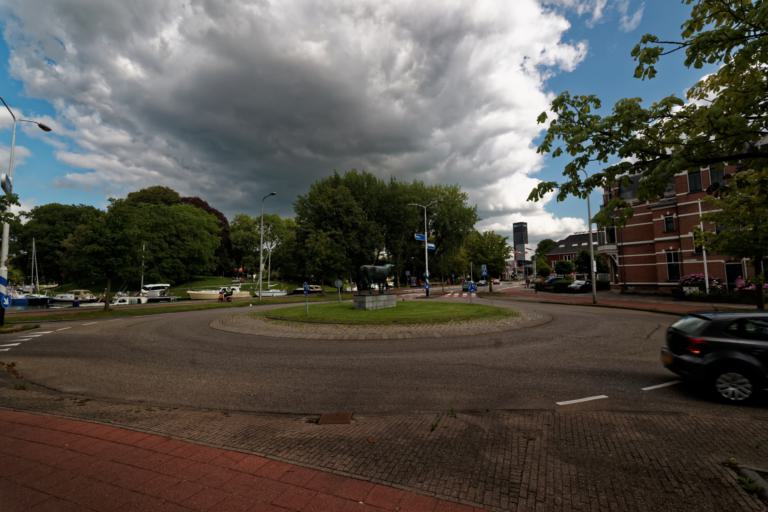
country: NL
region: Friesland
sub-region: Gemeente Leeuwarden
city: Bilgaard
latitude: 53.2041
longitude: 5.7869
